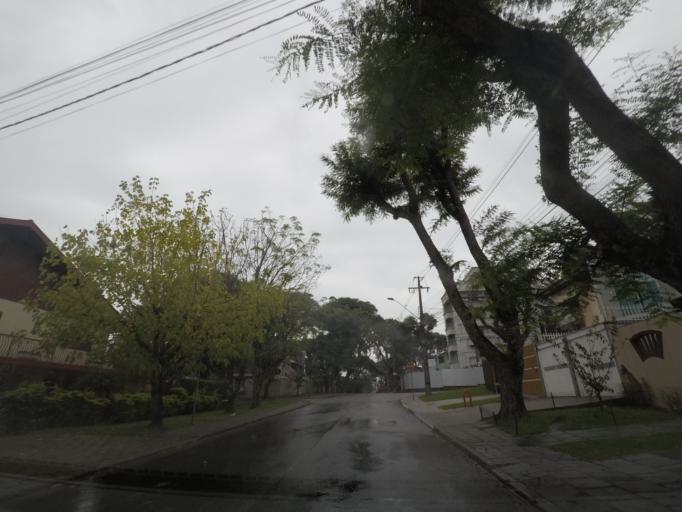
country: BR
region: Parana
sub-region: Curitiba
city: Curitiba
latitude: -25.4770
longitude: -49.3029
